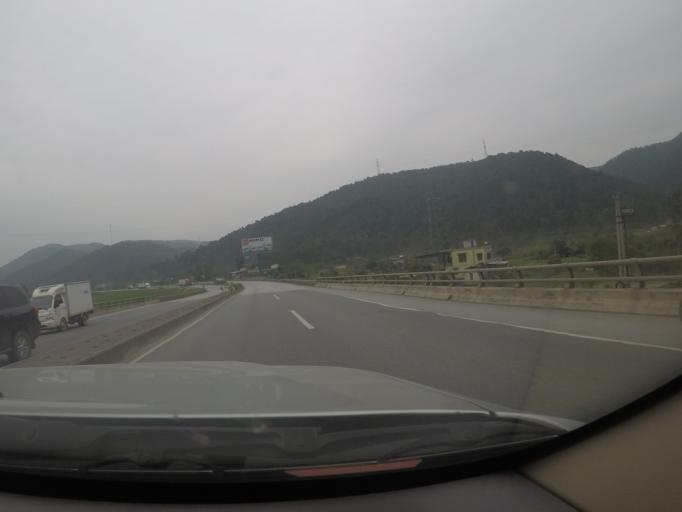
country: VN
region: Nghe An
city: Quan Hanh
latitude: 18.8742
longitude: 105.6169
